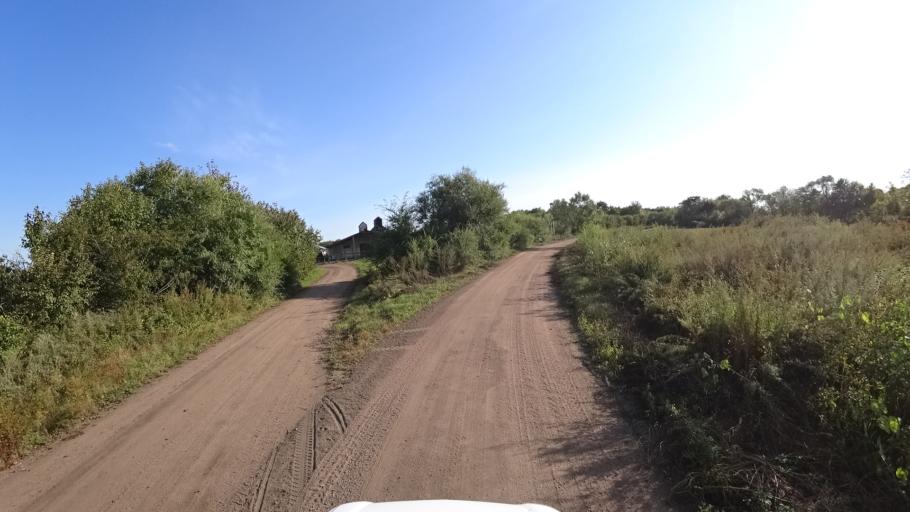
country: RU
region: Amur
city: Arkhara
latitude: 49.3502
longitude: 130.1009
